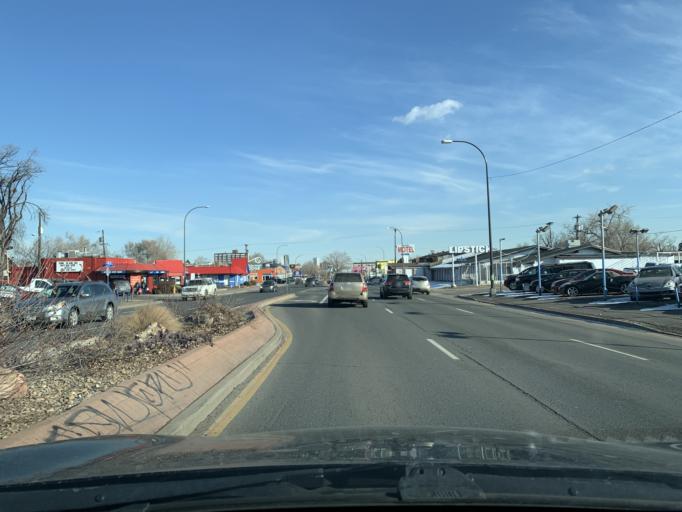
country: US
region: Colorado
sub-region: Jefferson County
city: Edgewater
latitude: 39.7403
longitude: -105.0597
